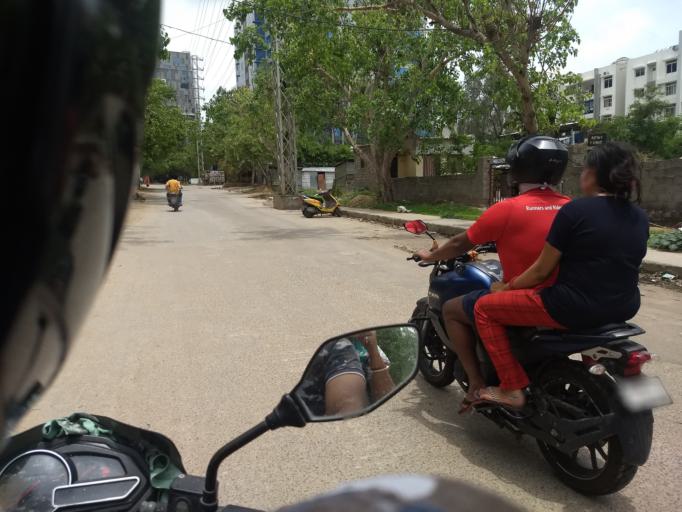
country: IN
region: Telangana
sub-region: Rangareddi
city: Kukatpalli
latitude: 17.4604
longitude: 78.3691
